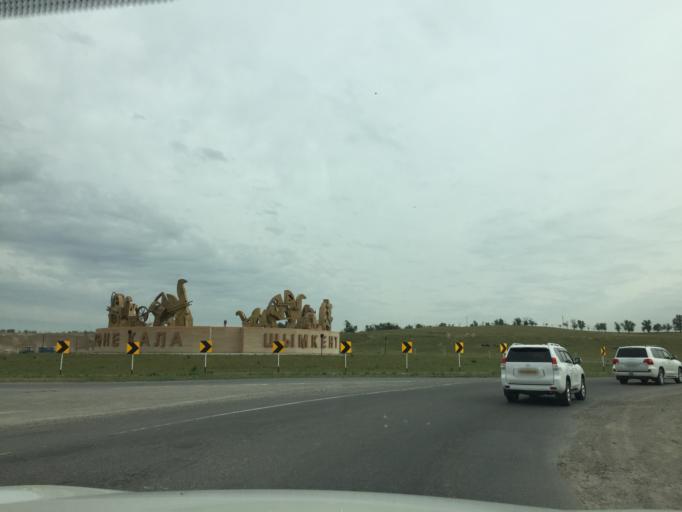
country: KZ
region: Ongtustik Qazaqstan
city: Shymkent
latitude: 42.4121
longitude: 69.6342
